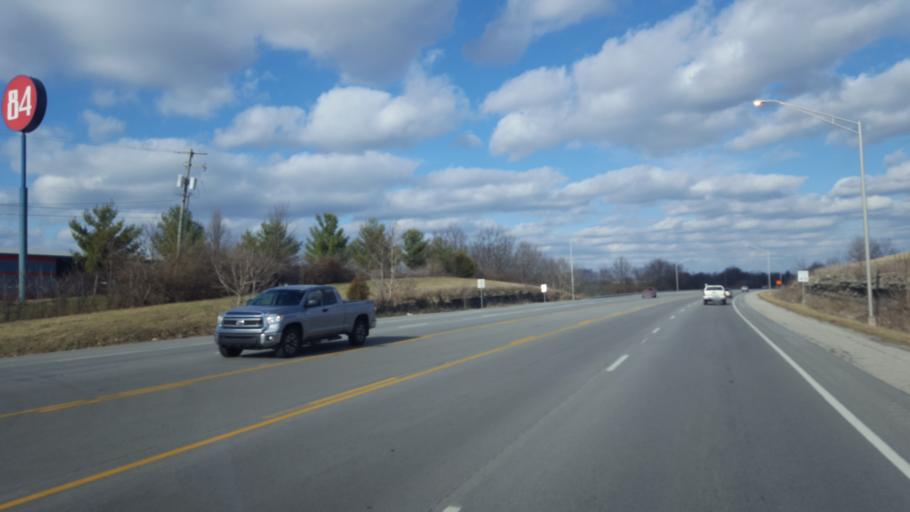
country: US
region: Kentucky
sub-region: Scott County
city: Georgetown
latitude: 38.2335
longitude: -84.5344
